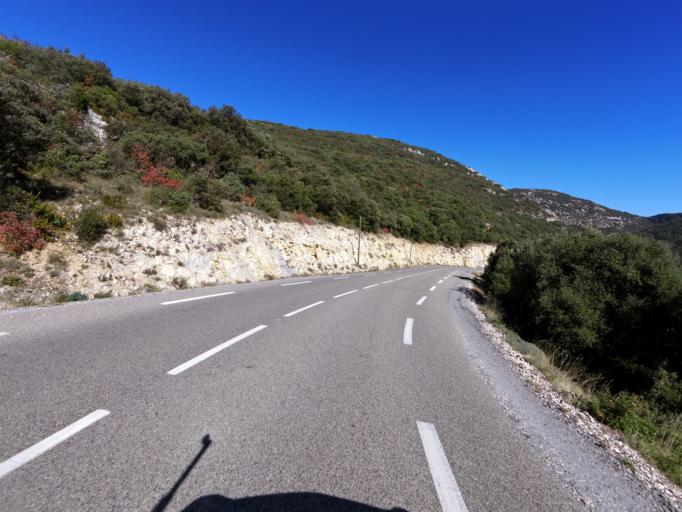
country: FR
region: Rhone-Alpes
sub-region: Departement de l'Ardeche
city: Ruoms
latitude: 44.4004
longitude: 4.4757
